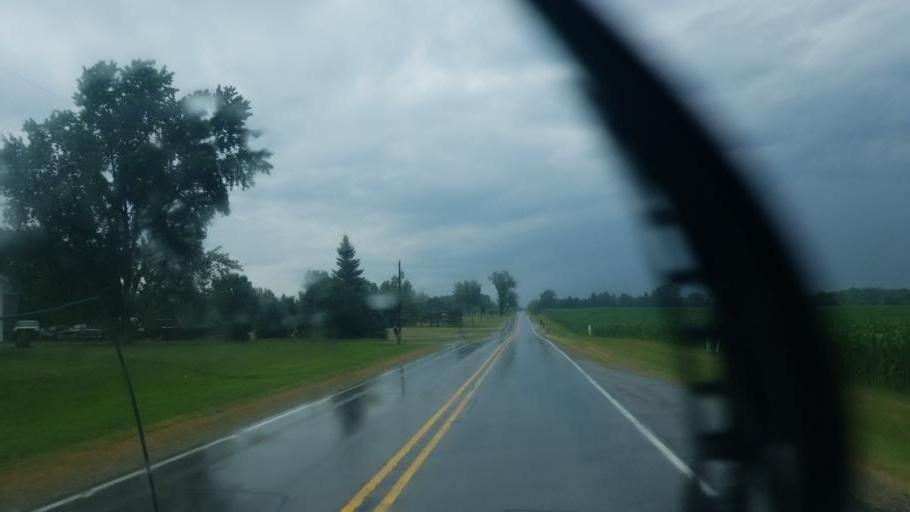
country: US
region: Indiana
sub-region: Steuben County
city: Hamilton
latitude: 41.4964
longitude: -84.8727
